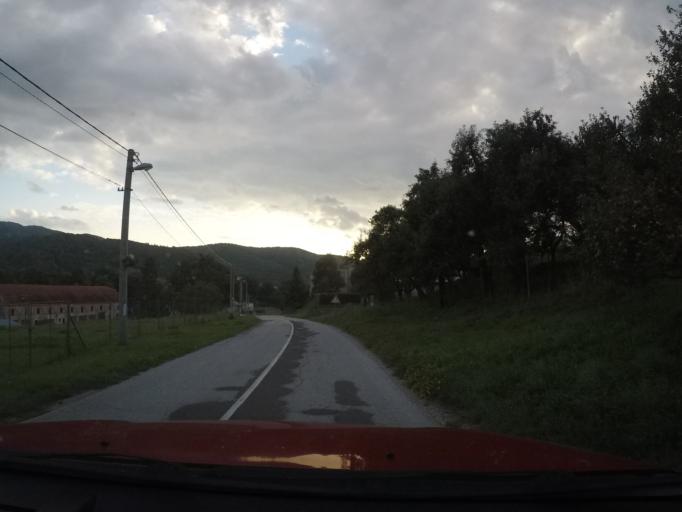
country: SK
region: Kosicky
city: Roznava
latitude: 48.6426
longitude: 20.6604
